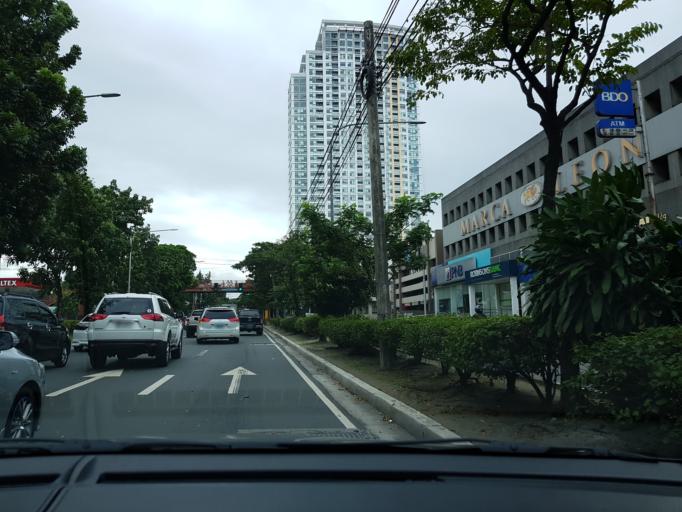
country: PH
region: Metro Manila
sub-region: San Juan
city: San Juan
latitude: 14.6023
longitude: 121.0459
